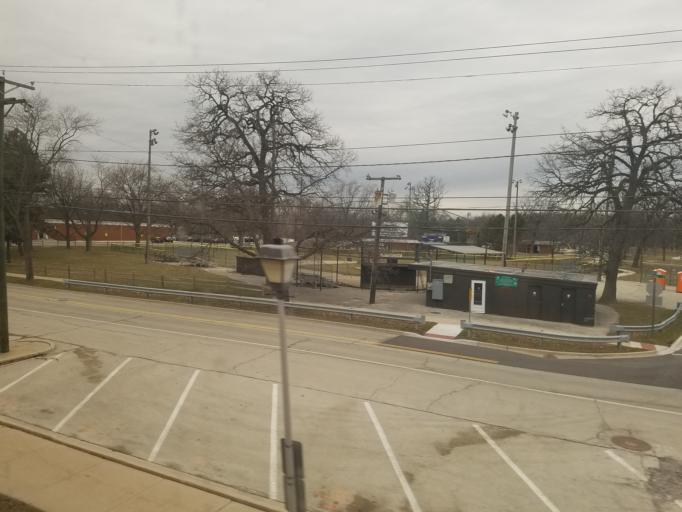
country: US
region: Illinois
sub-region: Cook County
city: Brookfield
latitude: 41.8228
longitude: -87.8390
